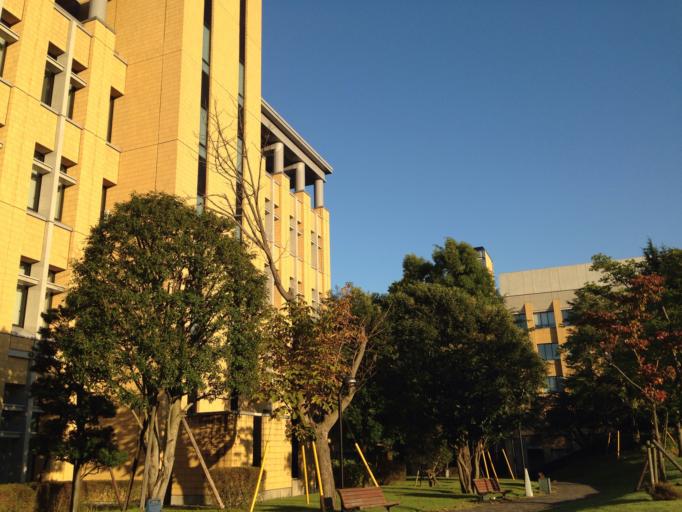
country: JP
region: Tokyo
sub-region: Machida-shi
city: Machida
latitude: 35.5661
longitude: 139.4021
